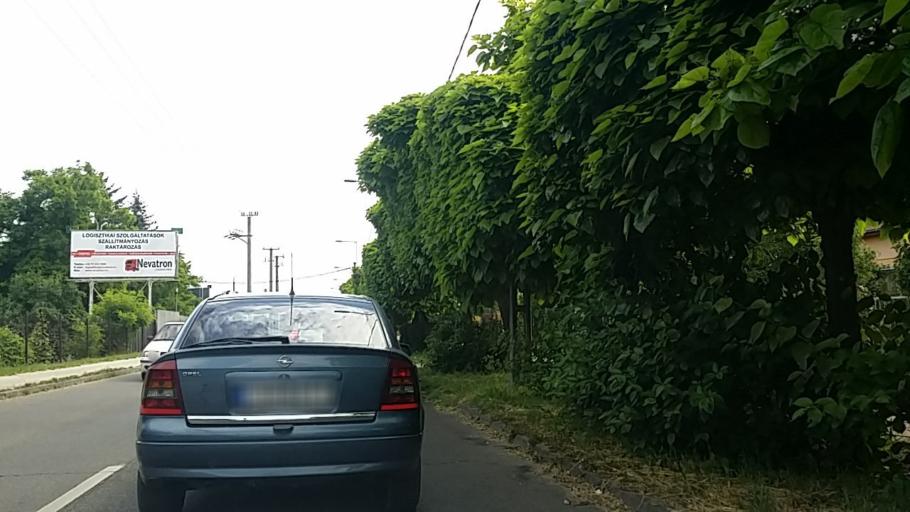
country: HU
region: Budapest
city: Budapest XXII. keruelet
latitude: 47.4018
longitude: 19.0576
